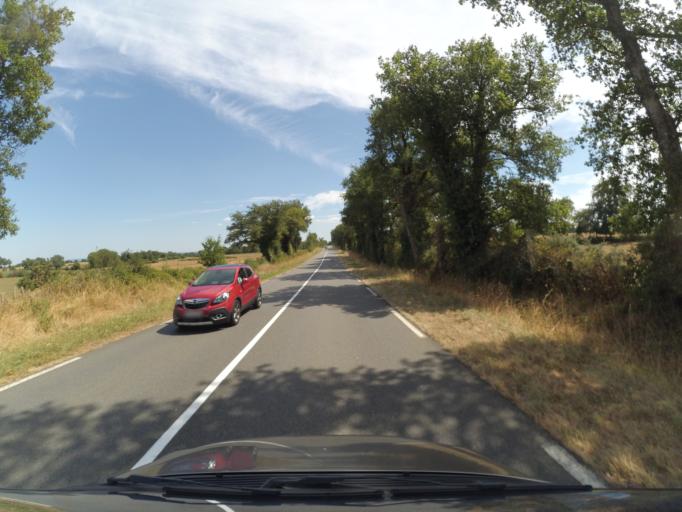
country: FR
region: Poitou-Charentes
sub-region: Departement de la Charente
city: Confolens
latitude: 46.0477
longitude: 0.6206
